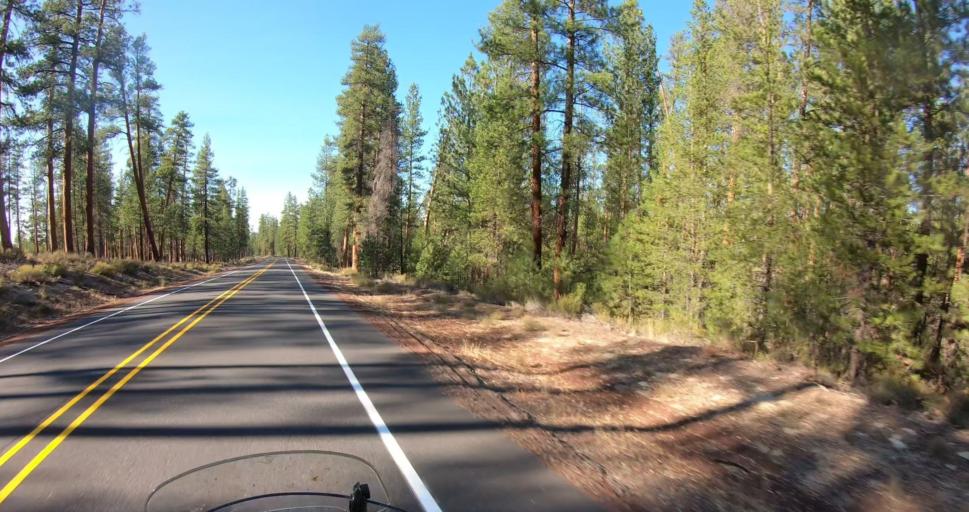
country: US
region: Oregon
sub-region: Deschutes County
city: La Pine
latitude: 43.4705
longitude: -121.3995
